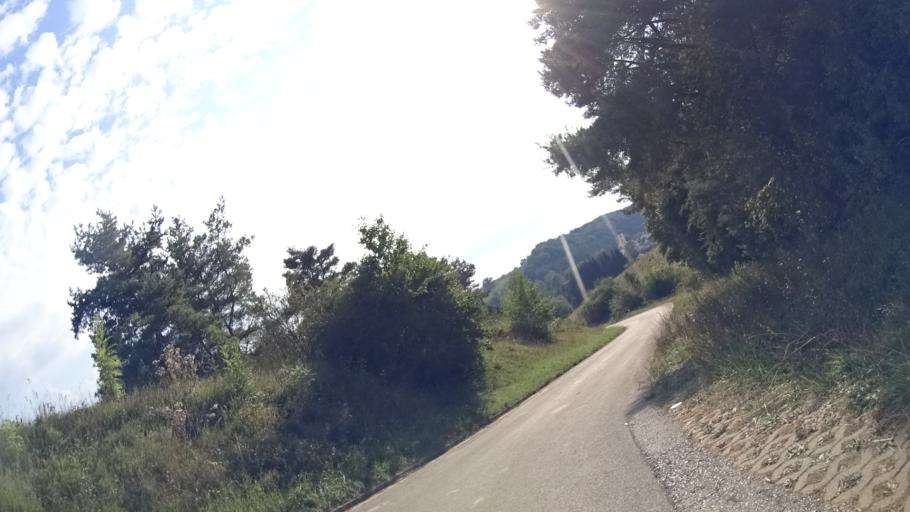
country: DE
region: Bavaria
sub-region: Upper Bavaria
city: Mindelstetten
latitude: 48.9045
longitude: 11.6424
